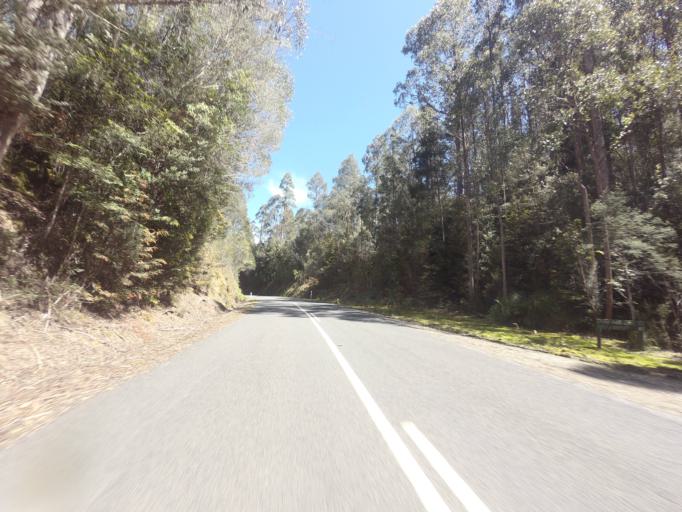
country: AU
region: Tasmania
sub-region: Huon Valley
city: Geeveston
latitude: -42.8194
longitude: 146.3045
